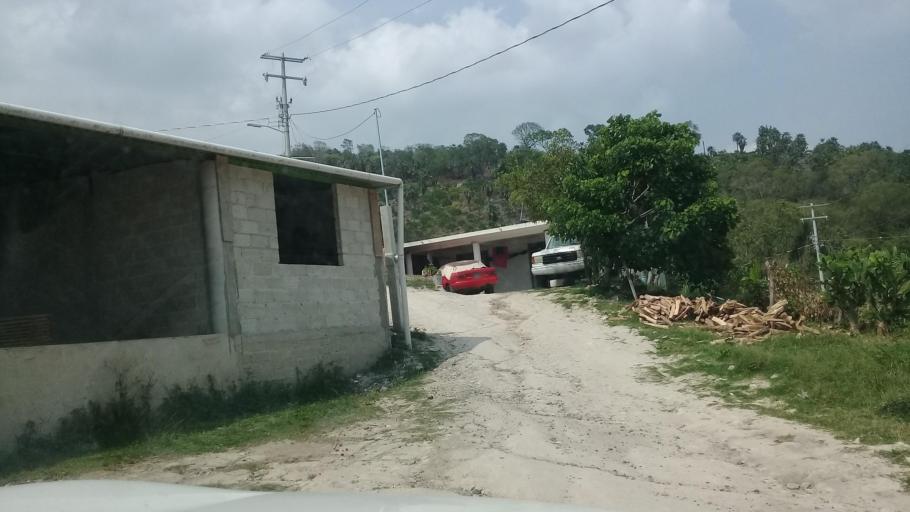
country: MX
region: Veracruz
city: Jalcomulco
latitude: 19.3972
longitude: -96.7878
